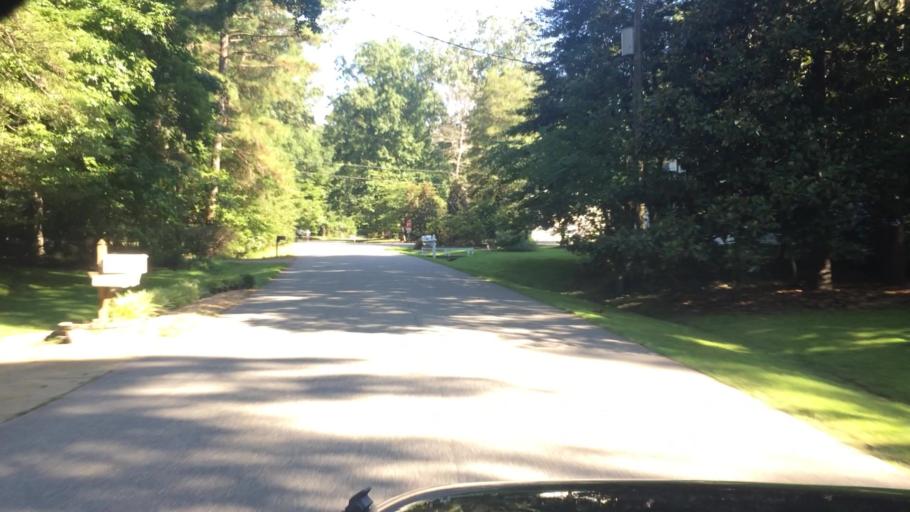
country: US
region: Virginia
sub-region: James City County
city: Williamsburg
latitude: 37.2406
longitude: -76.7978
